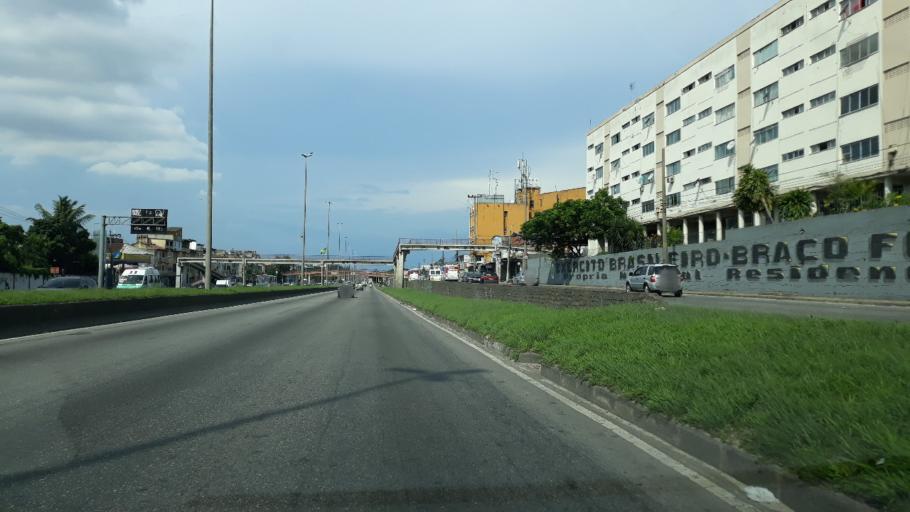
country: BR
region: Rio de Janeiro
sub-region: Sao Joao De Meriti
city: Sao Joao de Meriti
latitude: -22.8474
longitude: -43.3808
